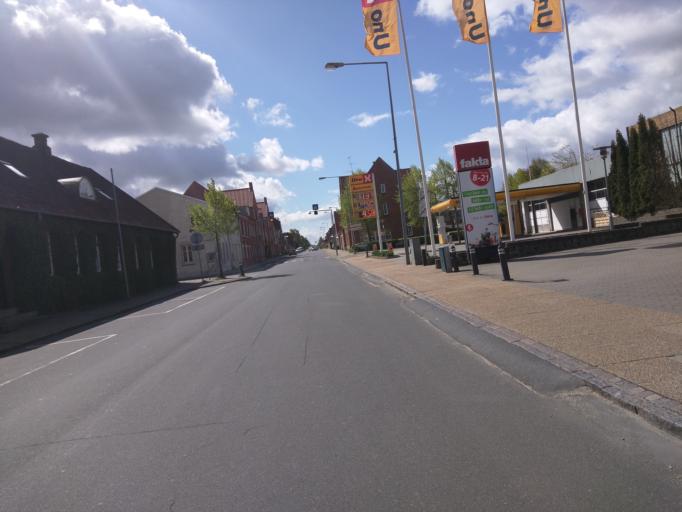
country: DK
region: Central Jutland
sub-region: Silkeborg Kommune
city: Kjellerup
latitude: 56.2877
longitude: 9.4310
